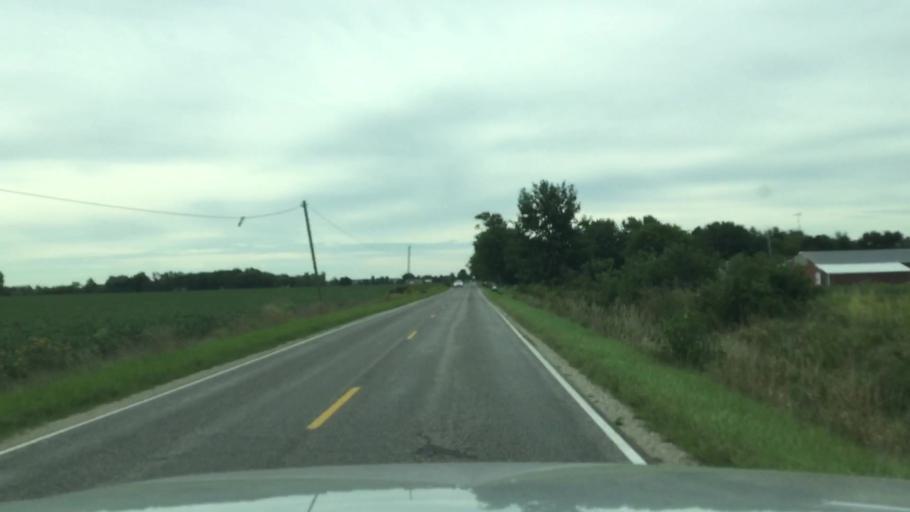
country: US
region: Michigan
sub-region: Shiawassee County
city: Durand
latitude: 43.0480
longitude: -83.9874
